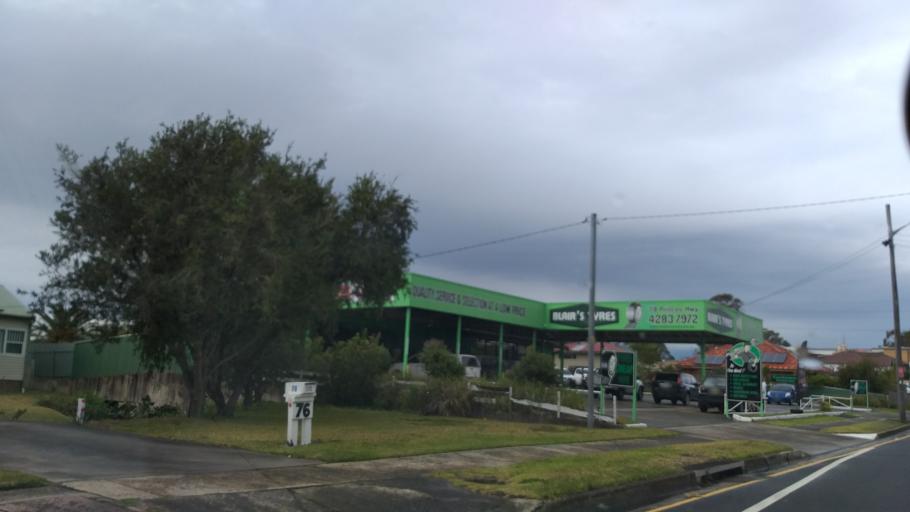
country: AU
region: New South Wales
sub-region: Wollongong
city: Corrimal
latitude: -34.3658
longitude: 150.8985
